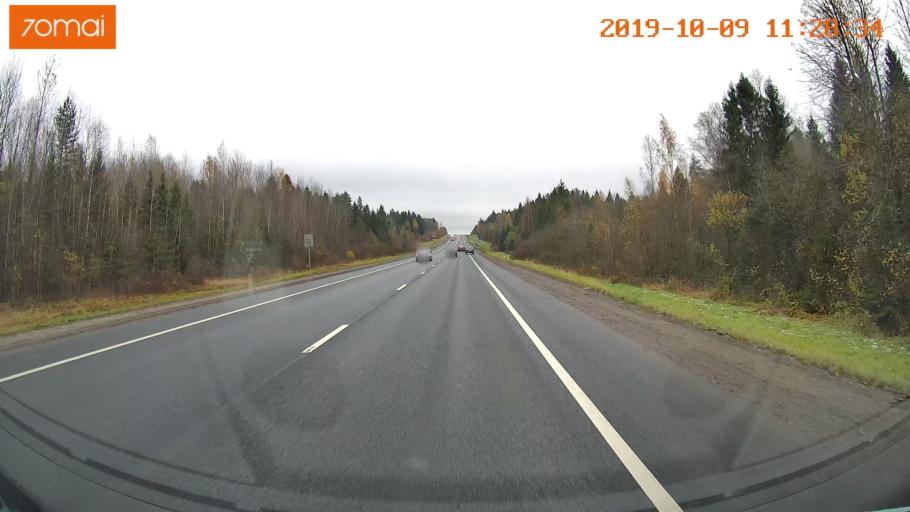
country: RU
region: Vologda
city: Vologda
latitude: 59.0673
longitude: 40.0401
